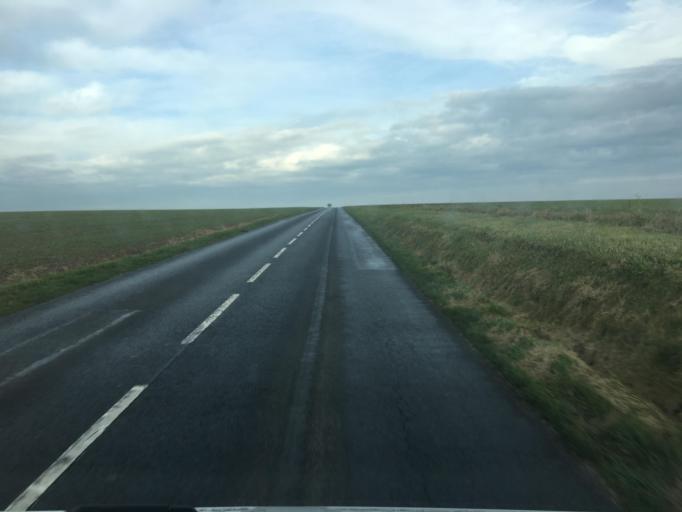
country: FR
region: Lower Normandy
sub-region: Departement du Calvados
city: Creully
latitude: 49.2985
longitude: -0.5460
